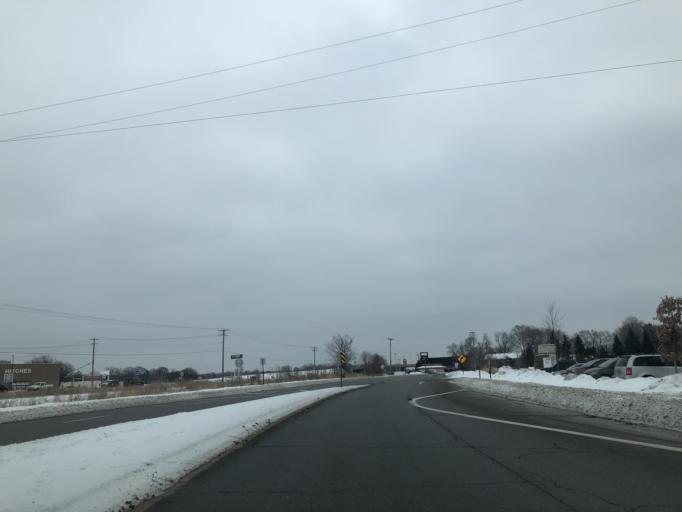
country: US
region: Minnesota
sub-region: Hennepin County
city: Brooklyn Park
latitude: 45.0828
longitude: -93.3778
